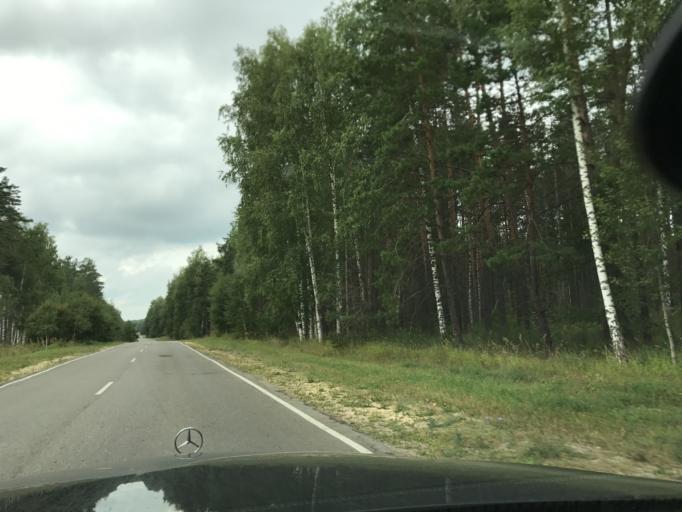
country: RU
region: Nizjnij Novgorod
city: Taremskoye
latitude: 56.0125
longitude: 42.9715
